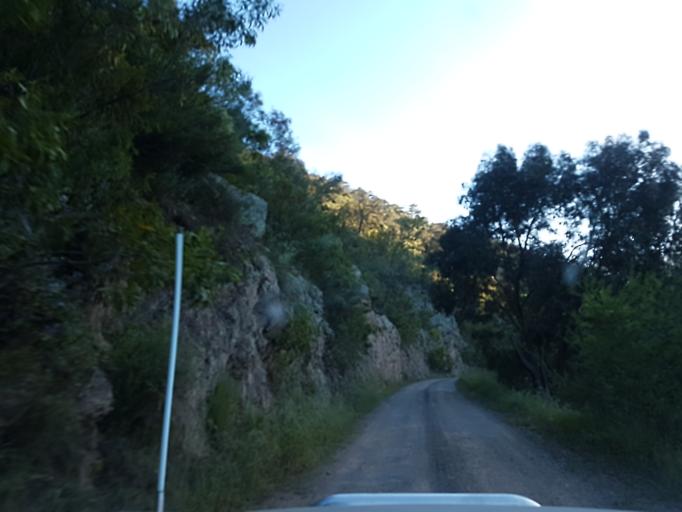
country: AU
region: Victoria
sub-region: Wellington
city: Heyfield
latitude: -37.4095
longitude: 147.0928
